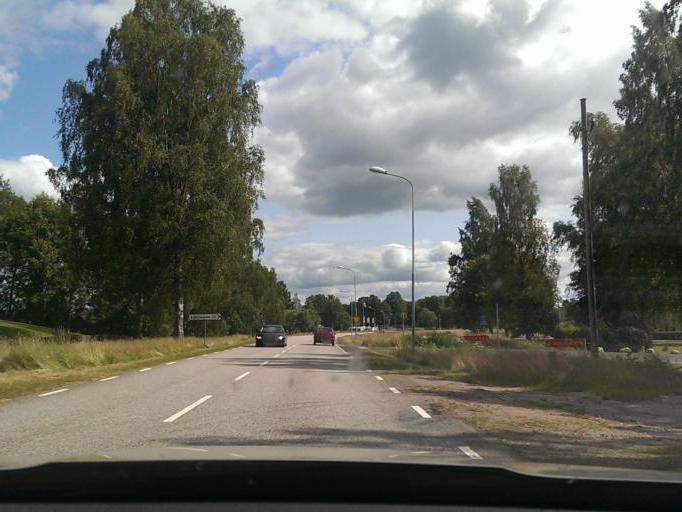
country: SE
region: Kronoberg
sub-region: Ljungby Kommun
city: Lagan
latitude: 56.9211
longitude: 13.9891
